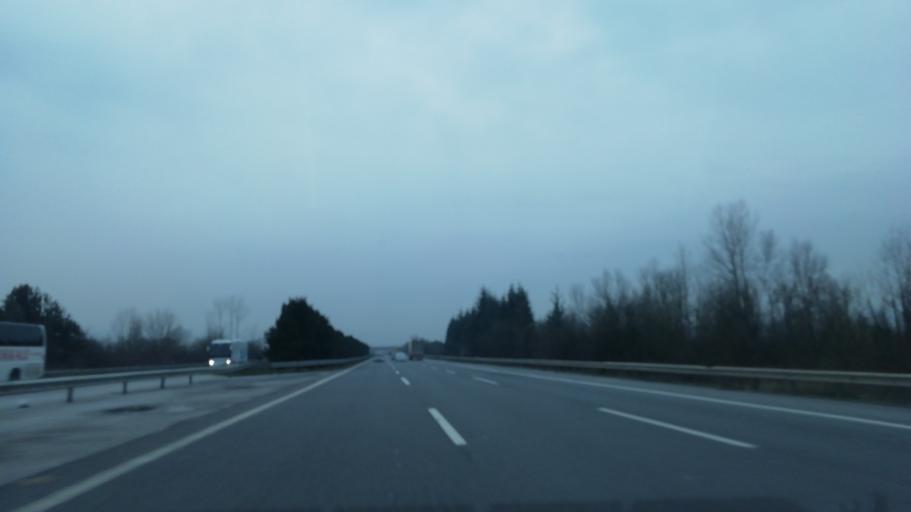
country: TR
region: Duzce
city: Cilimli
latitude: 40.8384
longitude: 31.0294
